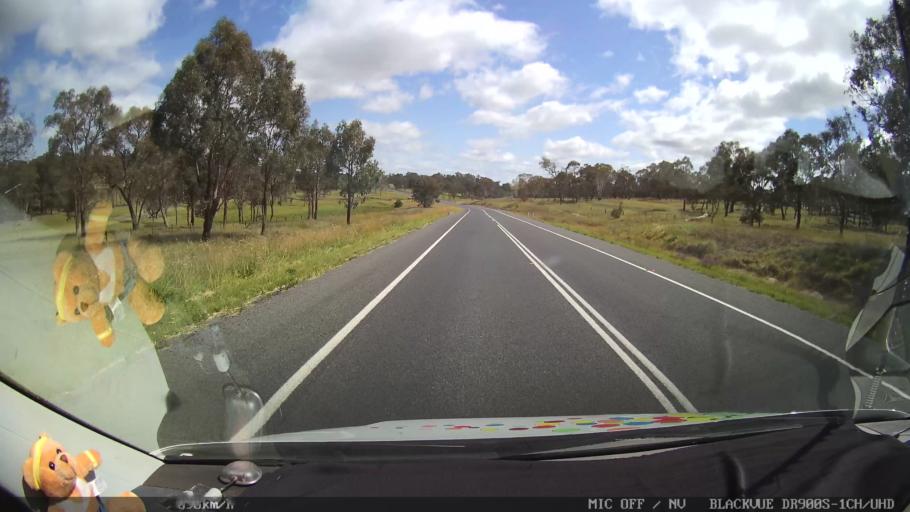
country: AU
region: New South Wales
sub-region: Glen Innes Severn
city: Glen Innes
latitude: -29.8974
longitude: 151.7339
